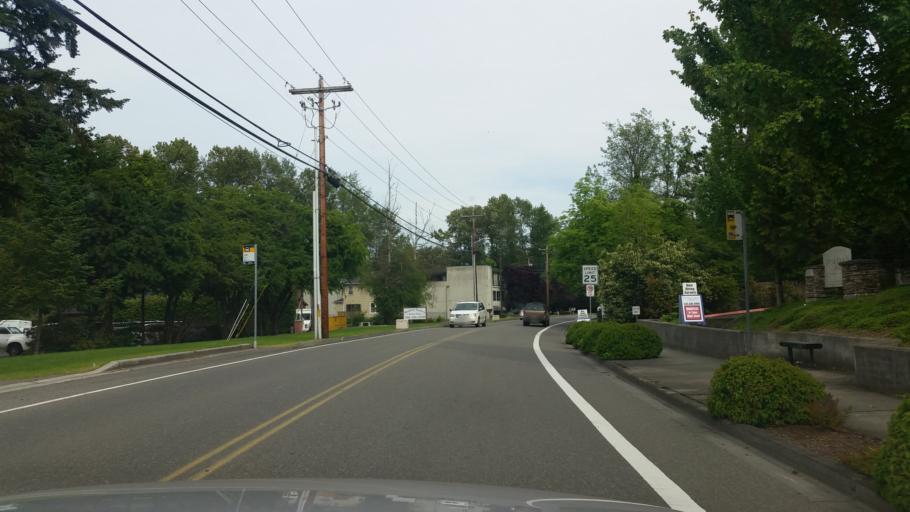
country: US
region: Washington
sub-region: King County
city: Bothell
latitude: 47.7561
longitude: -122.1998
